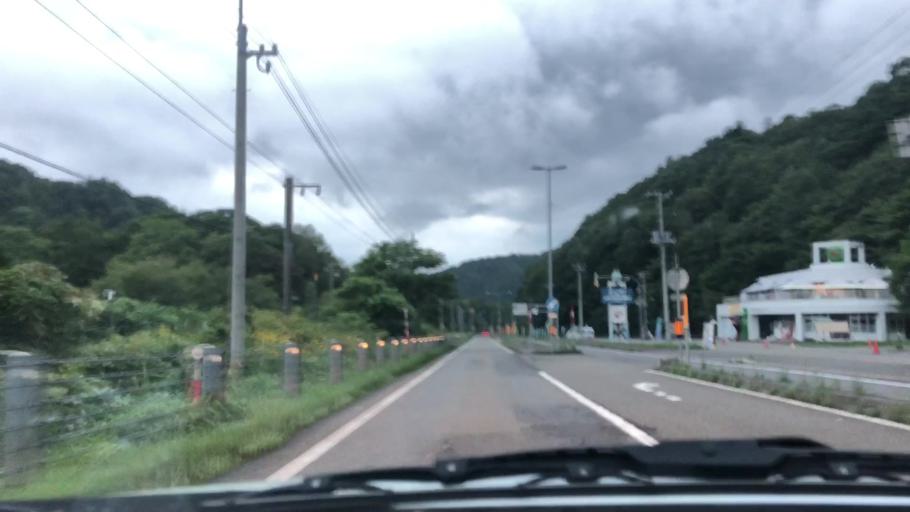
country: JP
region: Hokkaido
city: Chitose
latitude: 42.9129
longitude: 141.9700
